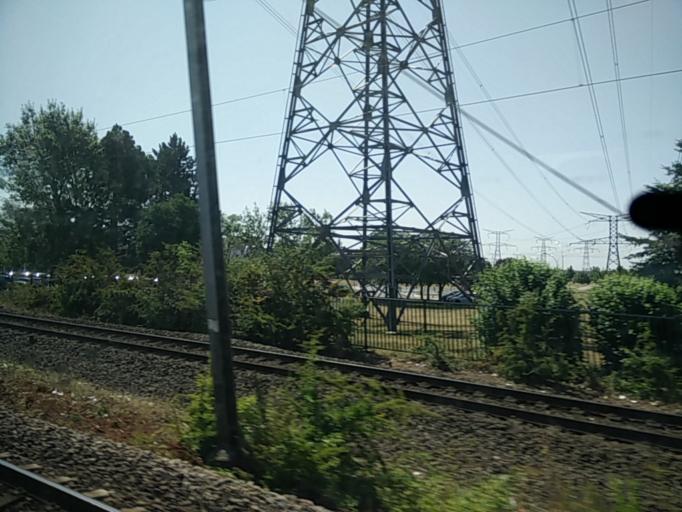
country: FR
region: Ile-de-France
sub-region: Departement de Seine-et-Marne
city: Roissy-en-Brie
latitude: 48.7965
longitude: 2.6482
